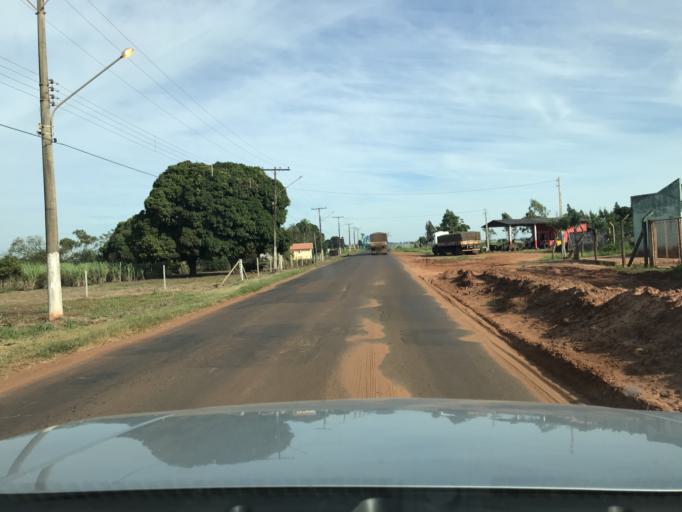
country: BR
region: Mato Grosso do Sul
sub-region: Iguatemi
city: Iguatemi
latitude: -23.6628
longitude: -54.5670
